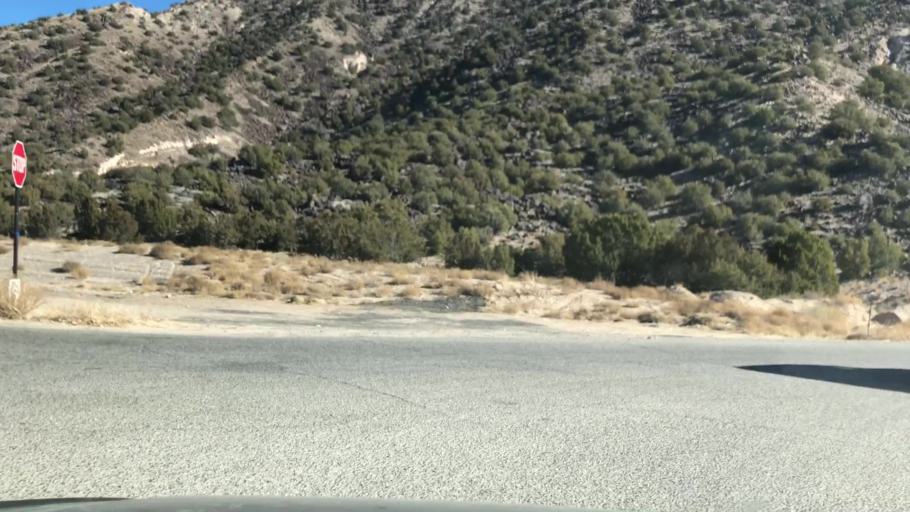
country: US
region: New Mexico
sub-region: Rio Arriba County
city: Ohkay Owingeh
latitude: 36.0964
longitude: -106.1301
